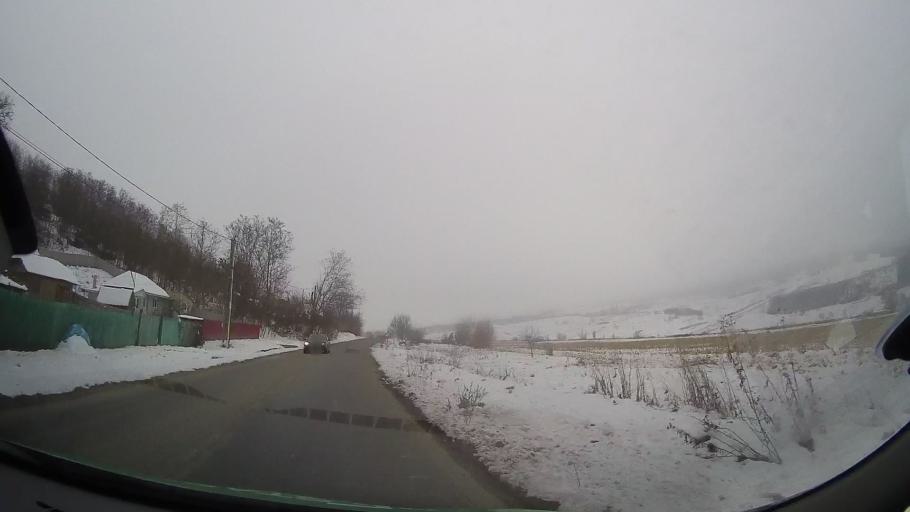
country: RO
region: Bacau
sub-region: Comuna Vultureni
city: Vultureni
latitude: 46.3399
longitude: 27.2907
